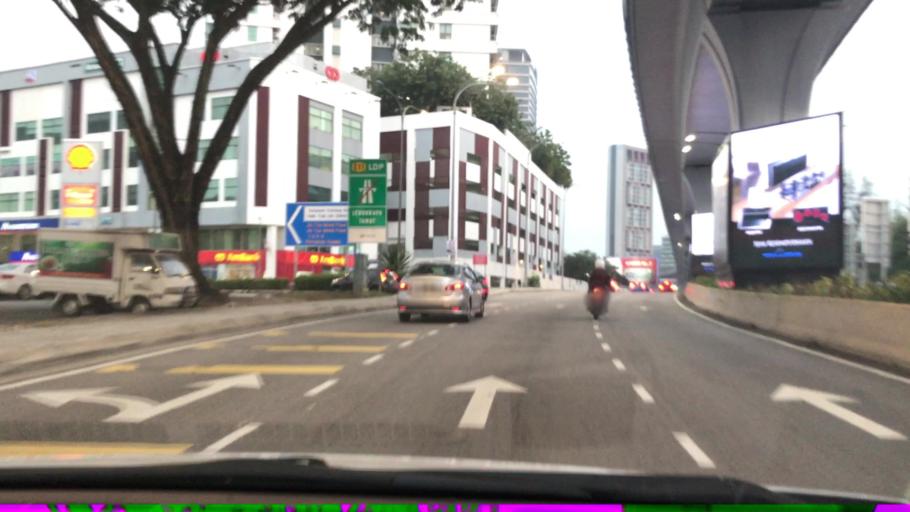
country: MY
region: Selangor
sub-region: Petaling
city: Petaling Jaya
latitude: 3.1411
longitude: 101.6263
